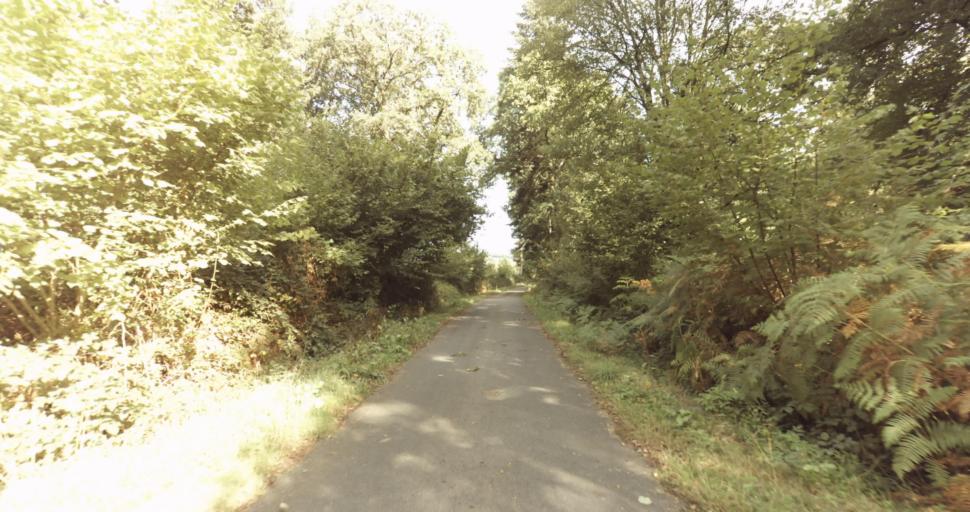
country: FR
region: Lower Normandy
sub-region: Departement de l'Orne
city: Gace
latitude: 48.8280
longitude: 0.2304
